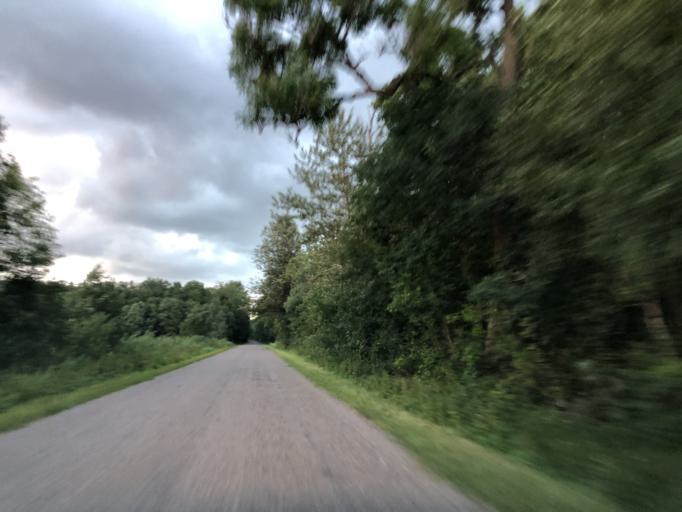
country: EE
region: Laeaene
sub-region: Ridala Parish
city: Uuemoisa
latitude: 58.9018
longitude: 23.6873
